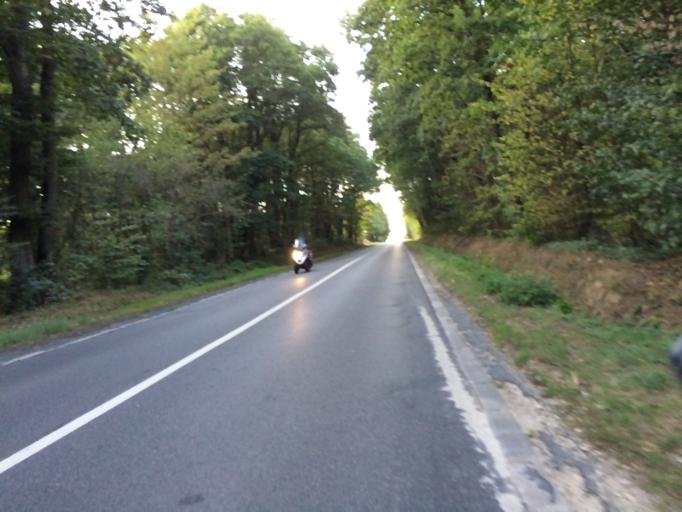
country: FR
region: Ile-de-France
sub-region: Departement de l'Essonne
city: Orsay
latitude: 48.6644
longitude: 2.1985
